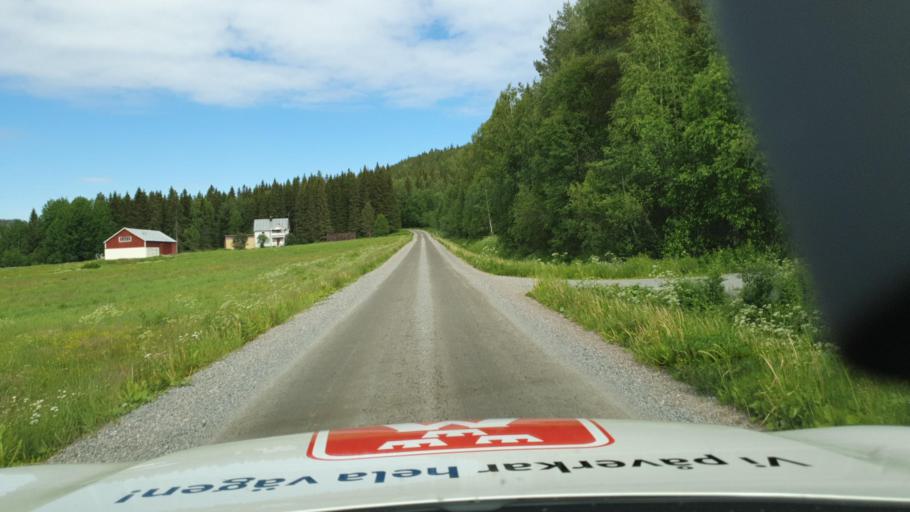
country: SE
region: Vaesterbotten
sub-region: Skelleftea Kommun
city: Forsbacka
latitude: 64.6367
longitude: 20.5458
